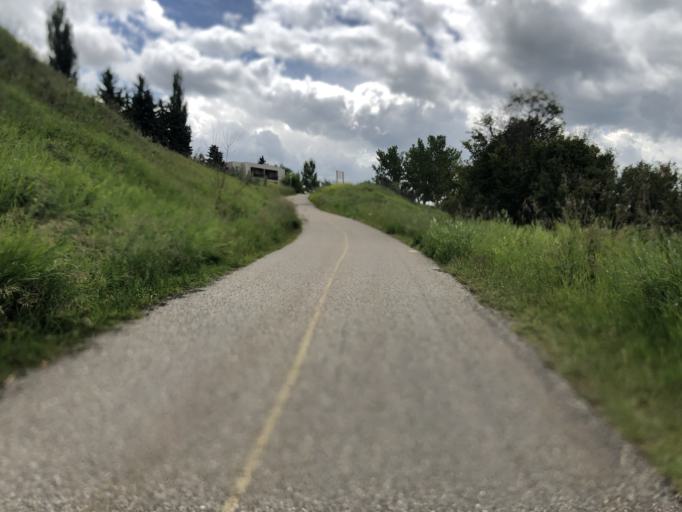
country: CA
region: Alberta
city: Calgary
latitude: 50.9983
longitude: -114.0228
